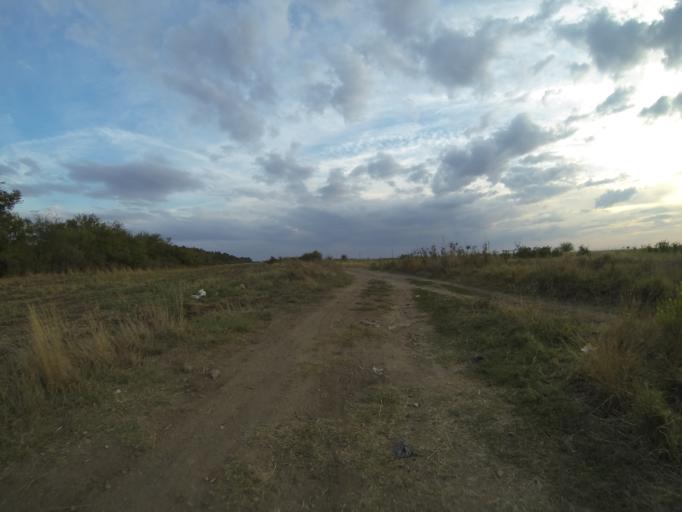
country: RO
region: Dolj
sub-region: Comuna Ceratu
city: Ceratu
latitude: 44.0869
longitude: 23.6751
